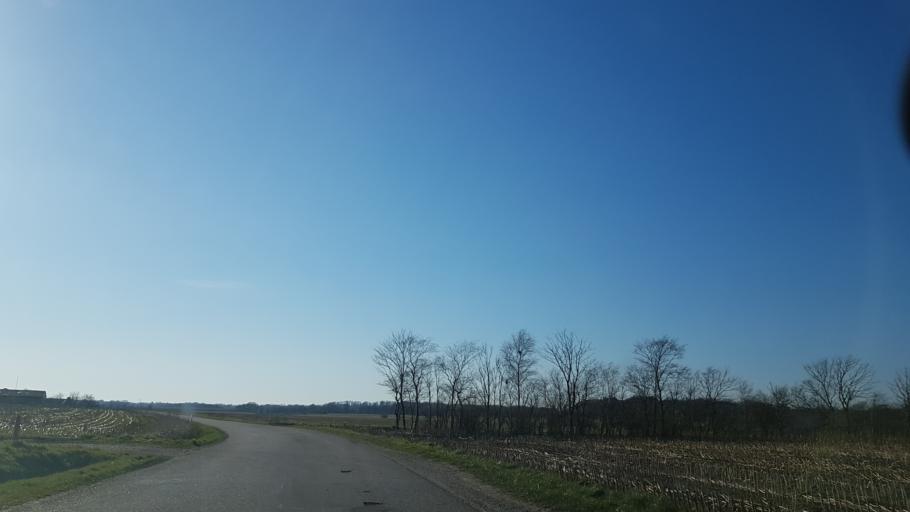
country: DK
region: South Denmark
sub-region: Vejen Kommune
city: Rodding
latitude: 55.3956
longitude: 9.0882
